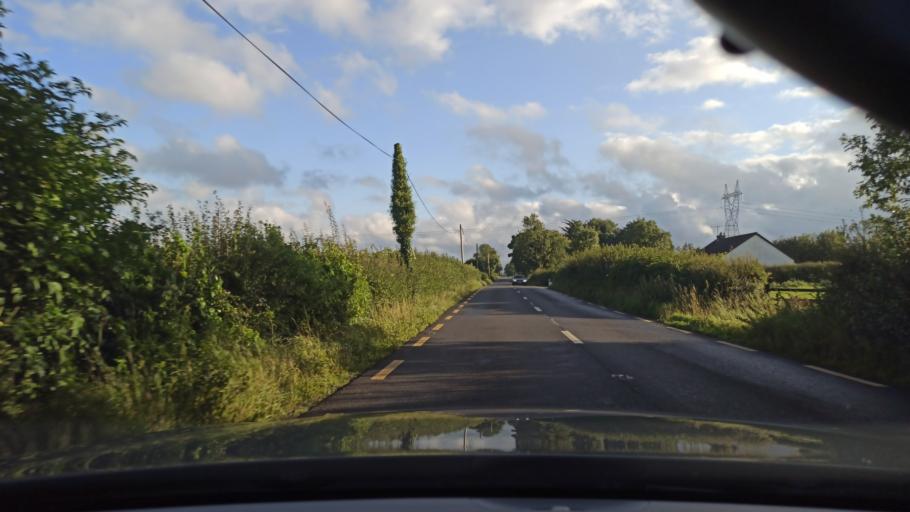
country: IE
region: Munster
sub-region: North Tipperary
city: Roscrea
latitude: 52.8971
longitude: -7.7993
